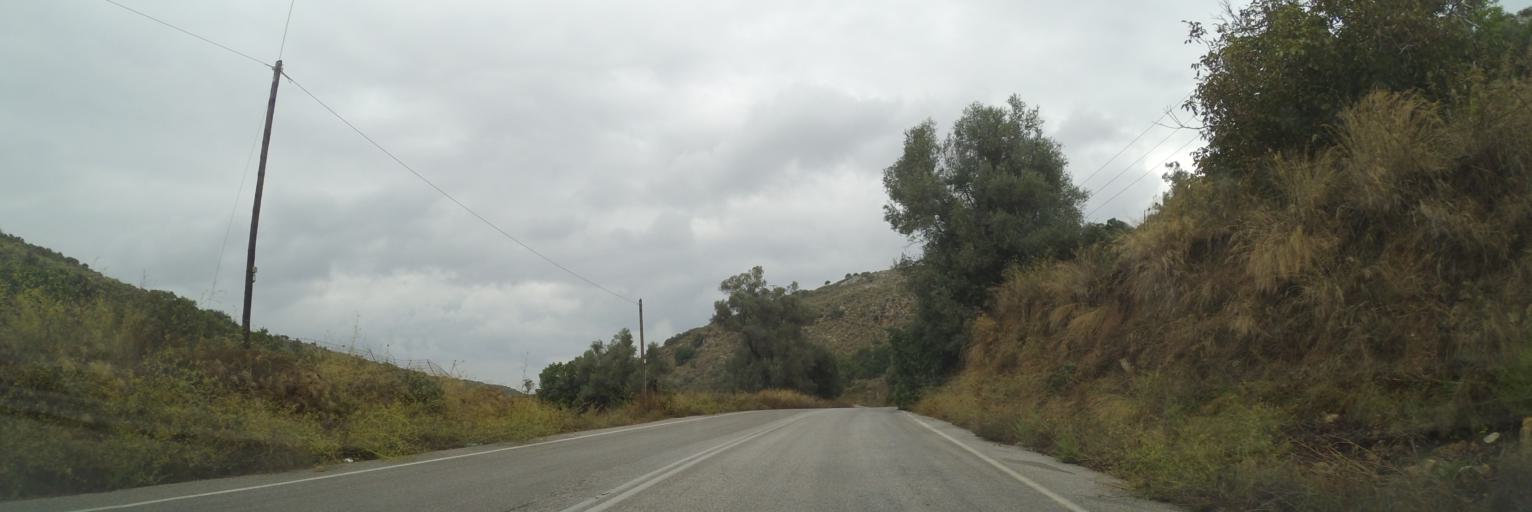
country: GR
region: Crete
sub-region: Nomos Rethymnis
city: Agia Foteini
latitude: 35.2944
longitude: 24.5649
